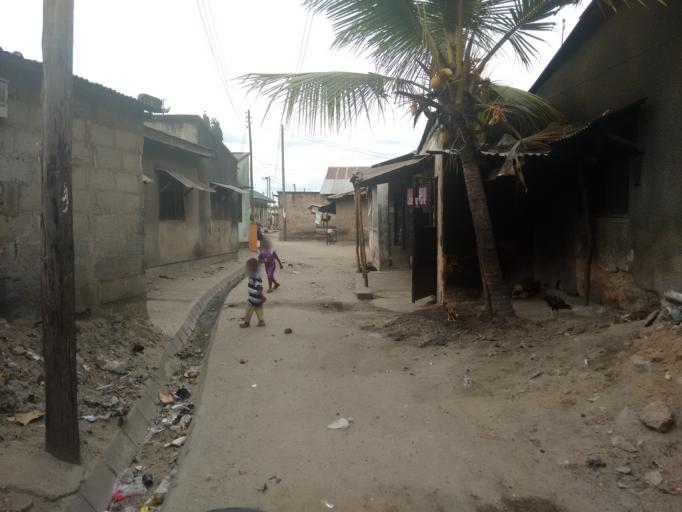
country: TZ
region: Dar es Salaam
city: Dar es Salaam
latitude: -6.8562
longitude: 39.2499
